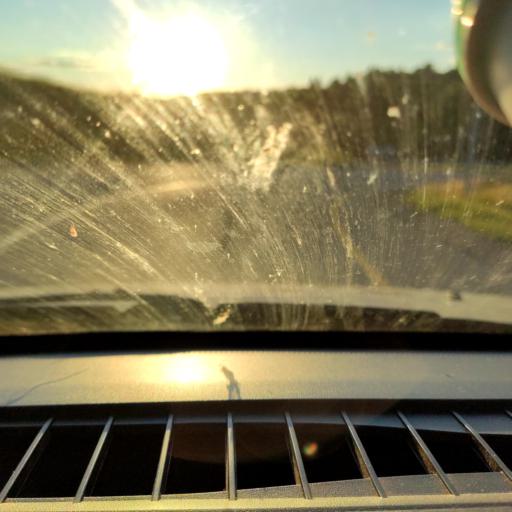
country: RU
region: Perm
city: Zvezdnyy
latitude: 57.7368
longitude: 56.3399
